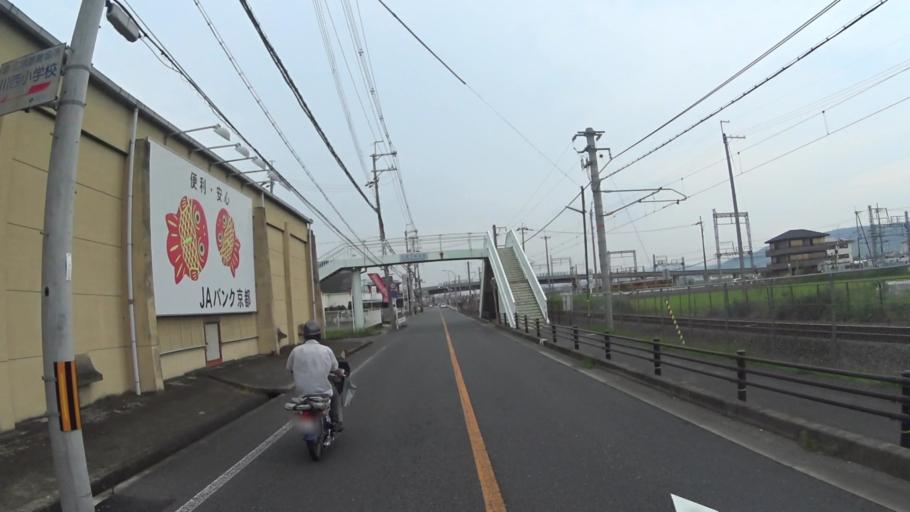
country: JP
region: Kyoto
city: Tanabe
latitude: 34.7660
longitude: 135.7912
